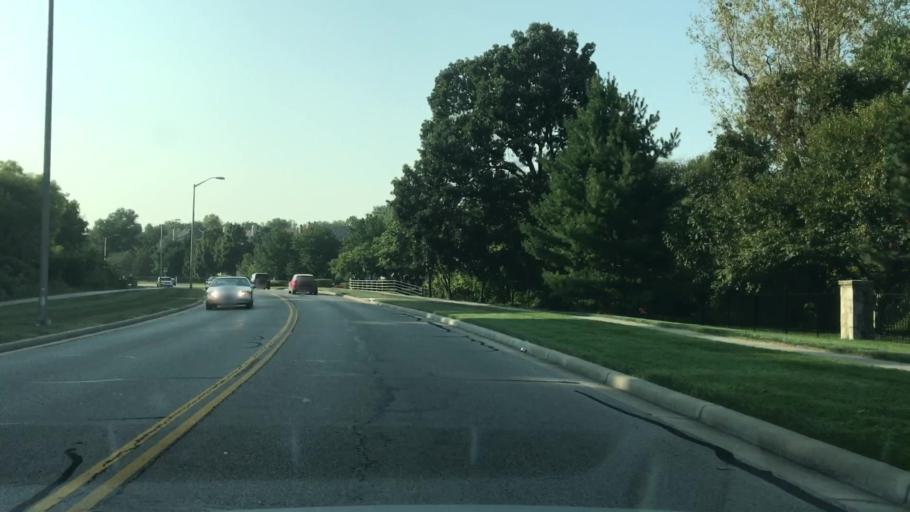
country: US
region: Kansas
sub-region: Johnson County
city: Lenexa
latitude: 38.9945
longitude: -94.7388
